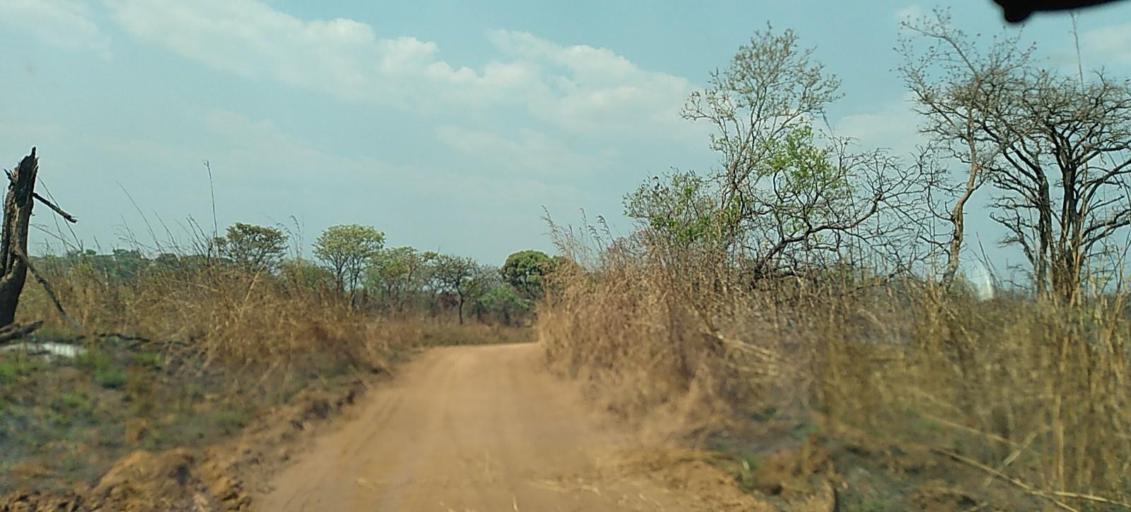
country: ZM
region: North-Western
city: Kasempa
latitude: -13.3072
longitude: 26.0690
